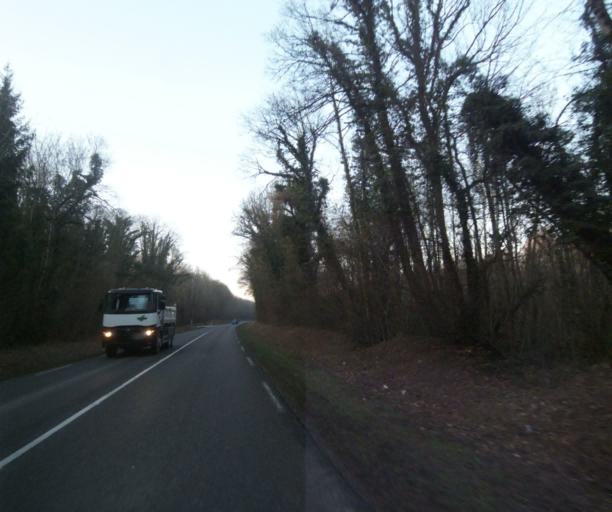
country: FR
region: Lorraine
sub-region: Departement de la Meuse
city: Ancerville
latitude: 48.6165
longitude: 4.9971
